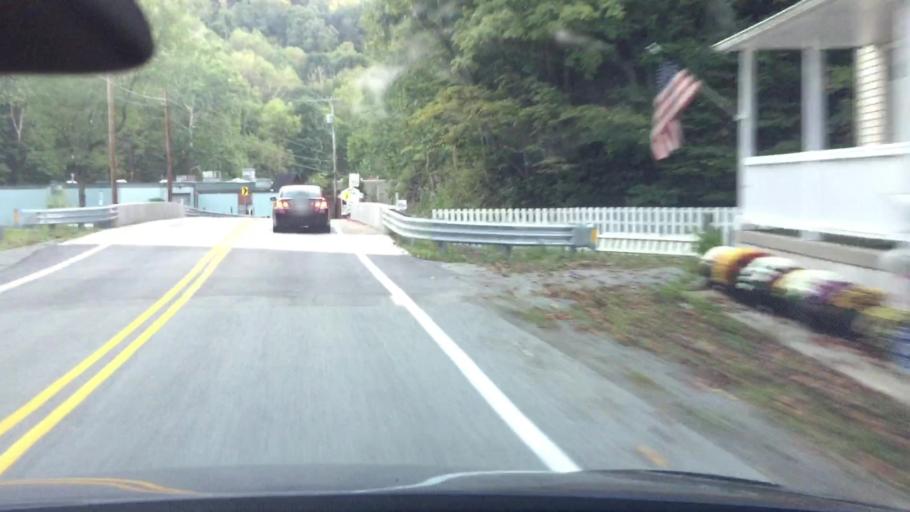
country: US
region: Pennsylvania
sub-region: Allegheny County
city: Etna
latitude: 40.5214
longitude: -79.9380
